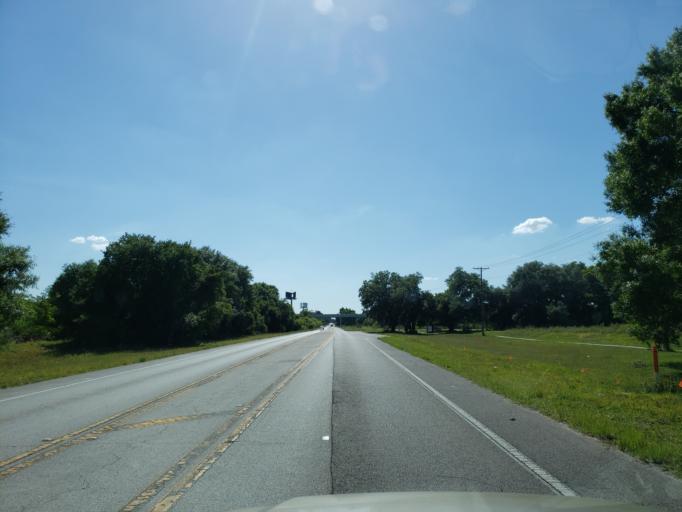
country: US
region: Florida
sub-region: Hillsborough County
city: Mango
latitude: 27.9736
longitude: -82.3215
